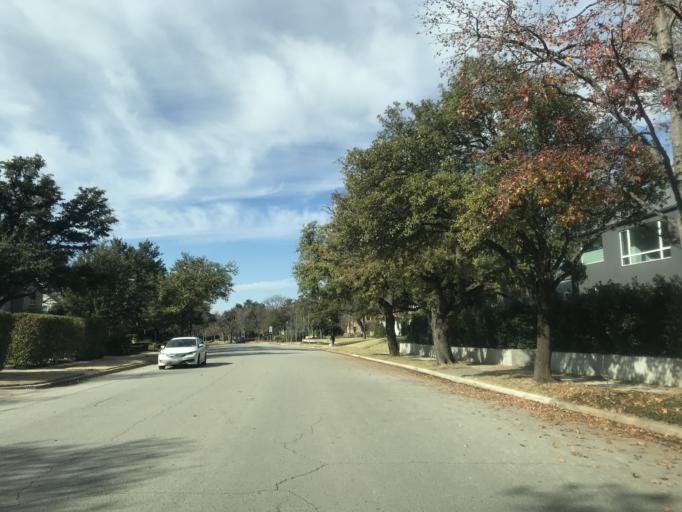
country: US
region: Texas
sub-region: Dallas County
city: Highland Park
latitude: 32.8267
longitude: -96.7930
